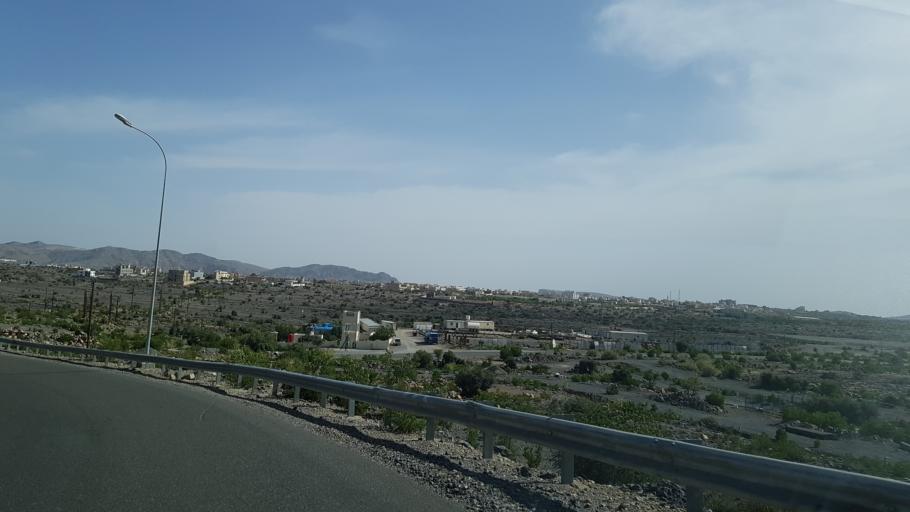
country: OM
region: Muhafazat ad Dakhiliyah
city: Izki
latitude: 23.0914
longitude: 57.6821
